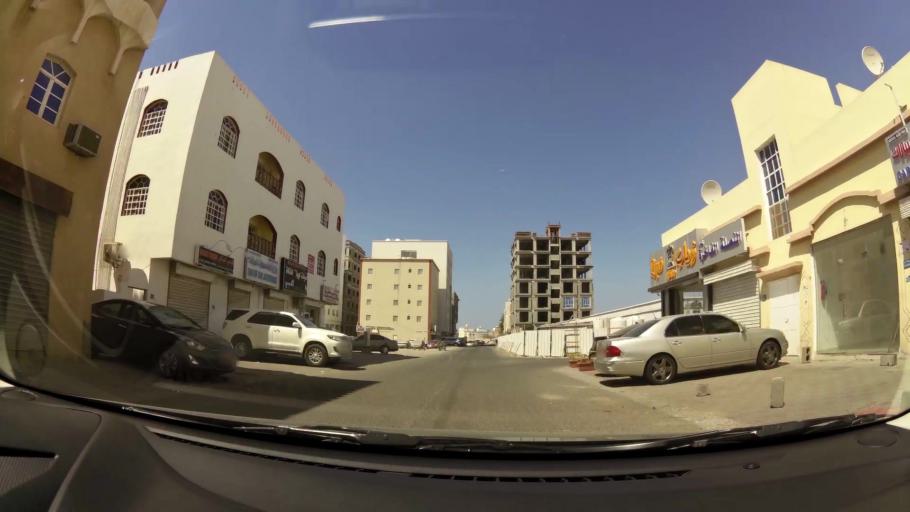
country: OM
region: Muhafazat Masqat
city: As Sib al Jadidah
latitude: 23.6257
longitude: 58.2194
